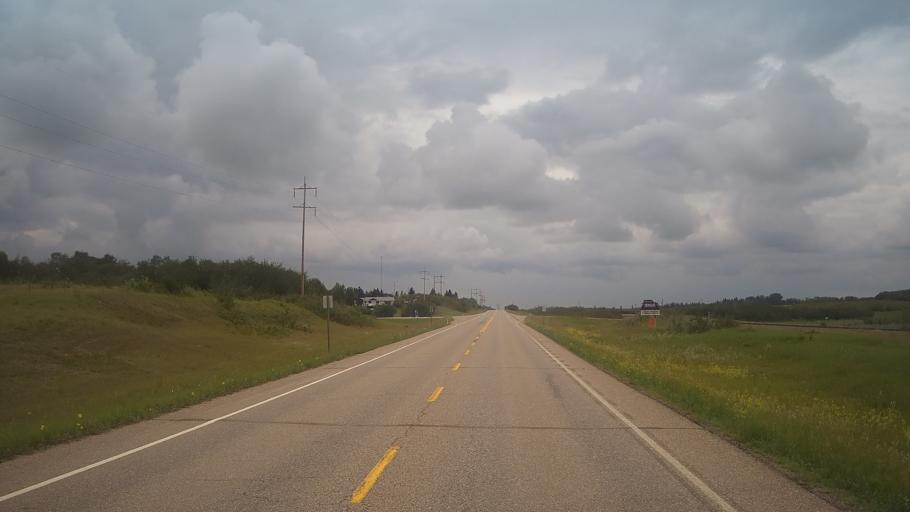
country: CA
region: Alberta
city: Wainwright
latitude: 52.5617
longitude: -111.0458
